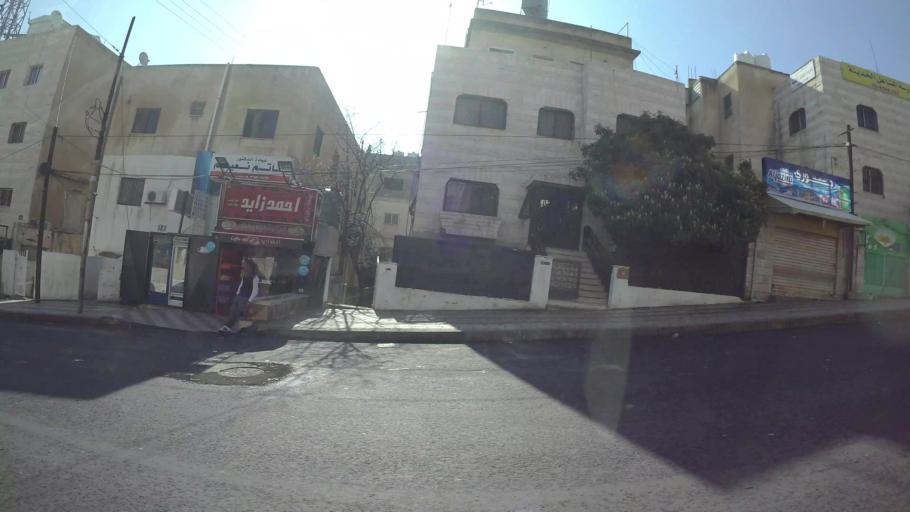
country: JO
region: Amman
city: Al Bunayyat ash Shamaliyah
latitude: 31.9317
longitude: 35.9066
